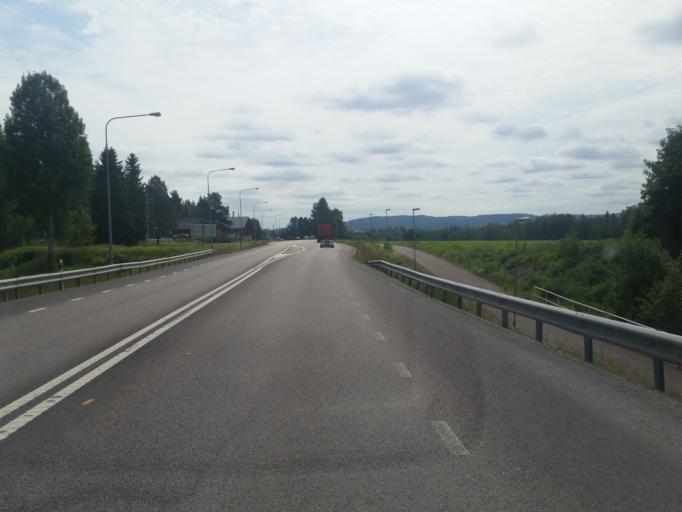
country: SE
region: Dalarna
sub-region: Gagnefs Kommun
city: Djuras
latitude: 60.5589
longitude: 15.1378
